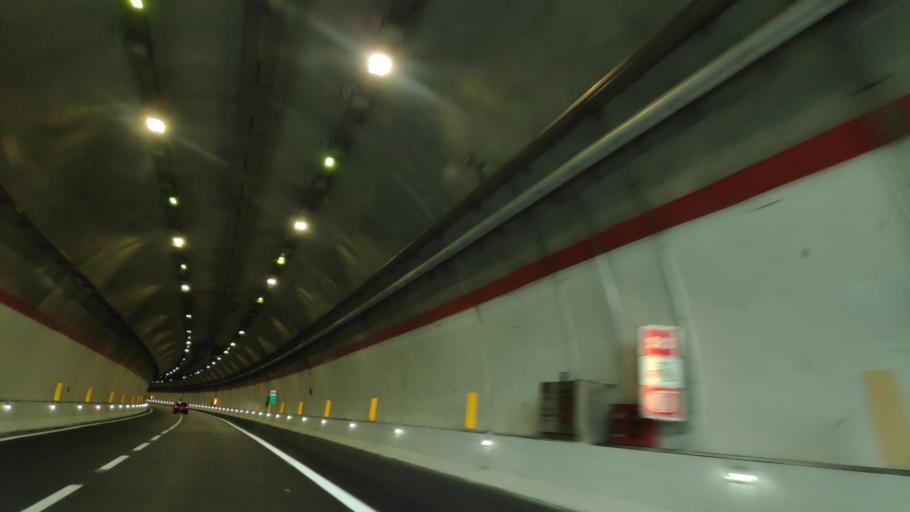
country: IT
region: Calabria
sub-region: Provincia di Reggio Calabria
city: Seminara
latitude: 38.3453
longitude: 15.8692
